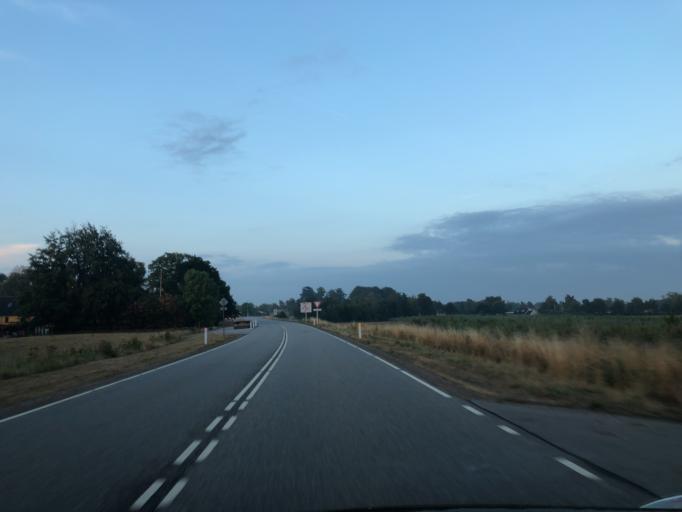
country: DK
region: Zealand
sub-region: Soro Kommune
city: Stenlille
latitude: 55.5928
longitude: 11.6583
